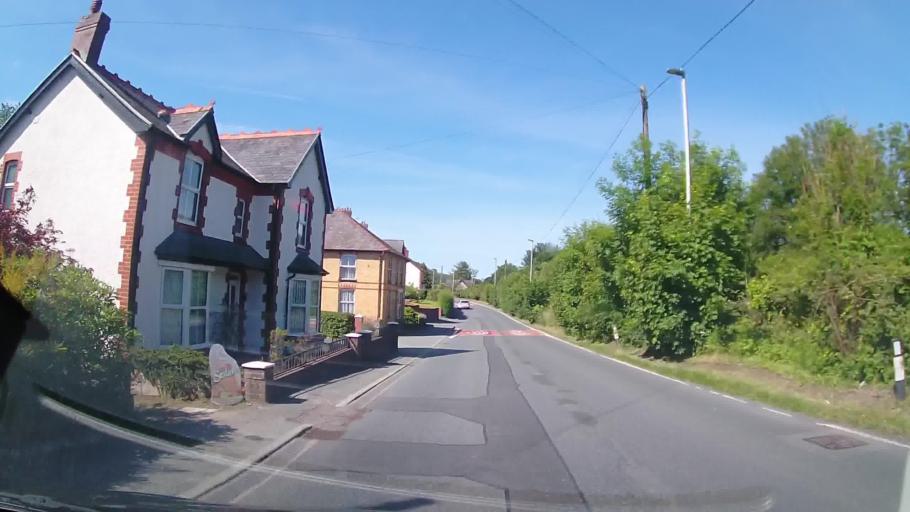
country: GB
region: Wales
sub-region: Gwynedd
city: Corris
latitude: 52.6241
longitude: -3.7452
